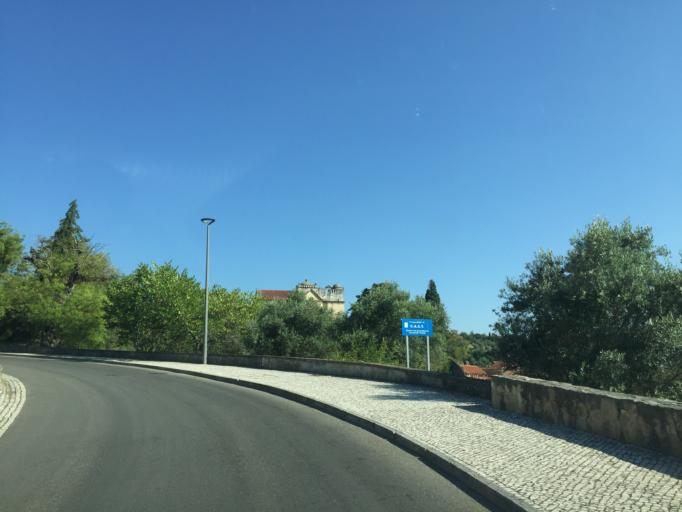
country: PT
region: Santarem
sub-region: Tomar
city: Tomar
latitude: 39.6047
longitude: -8.4161
